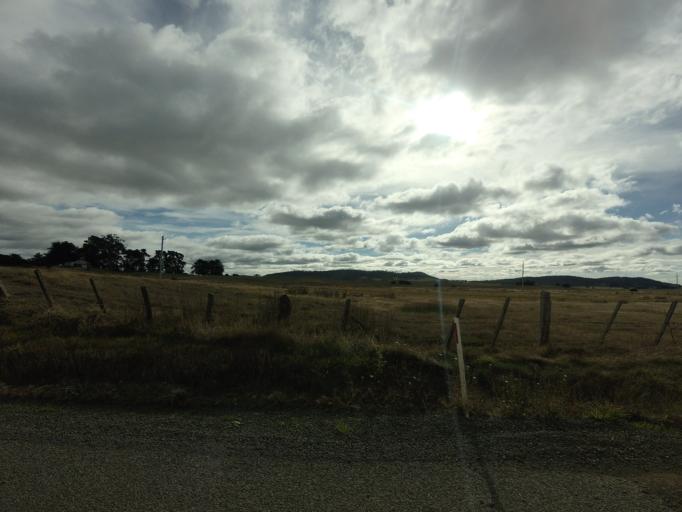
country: AU
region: Tasmania
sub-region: Brighton
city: Bridgewater
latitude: -42.4294
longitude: 147.3877
